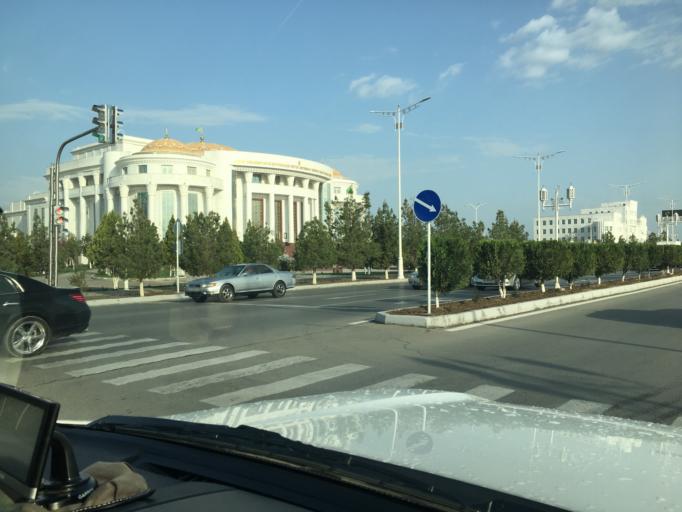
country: TM
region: Lebap
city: Turkmenabat
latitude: 39.0790
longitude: 63.5867
